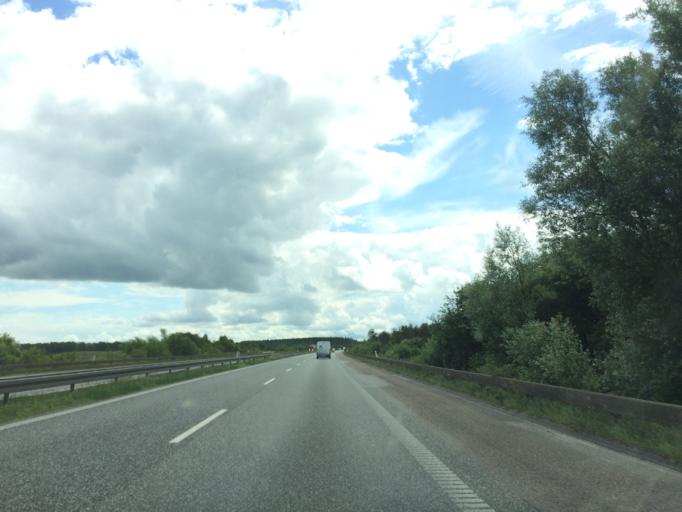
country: DK
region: North Denmark
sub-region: Mariagerfjord Kommune
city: Hobro
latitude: 56.6517
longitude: 9.7377
